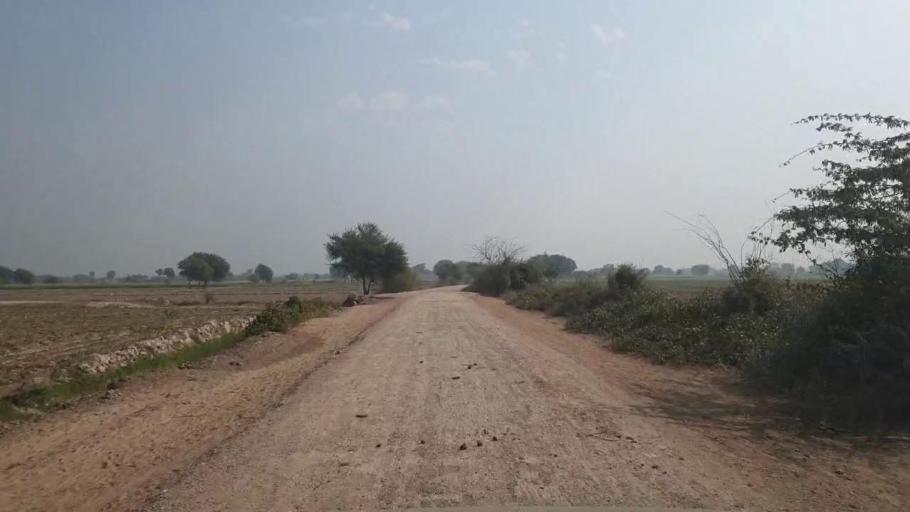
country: PK
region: Sindh
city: Hala
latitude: 25.7631
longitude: 68.4295
